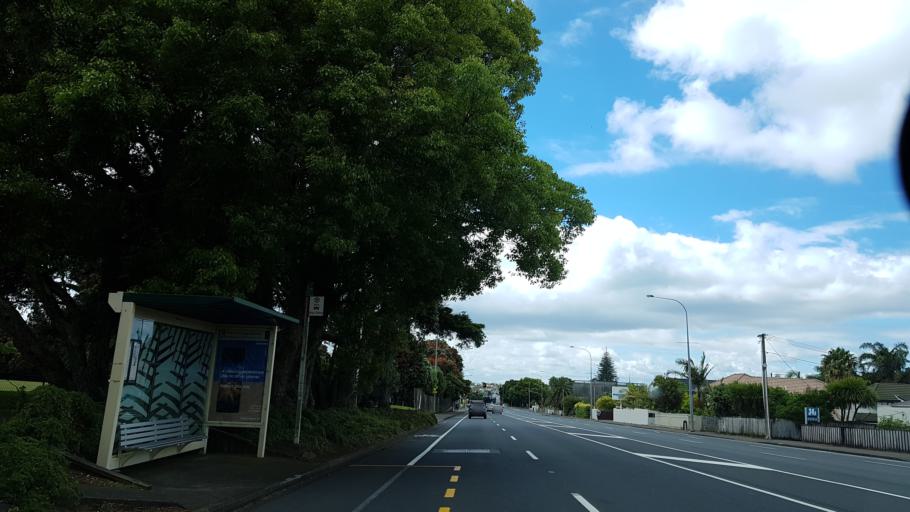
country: NZ
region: Auckland
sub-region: Auckland
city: North Shore
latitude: -36.7879
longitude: 174.7593
